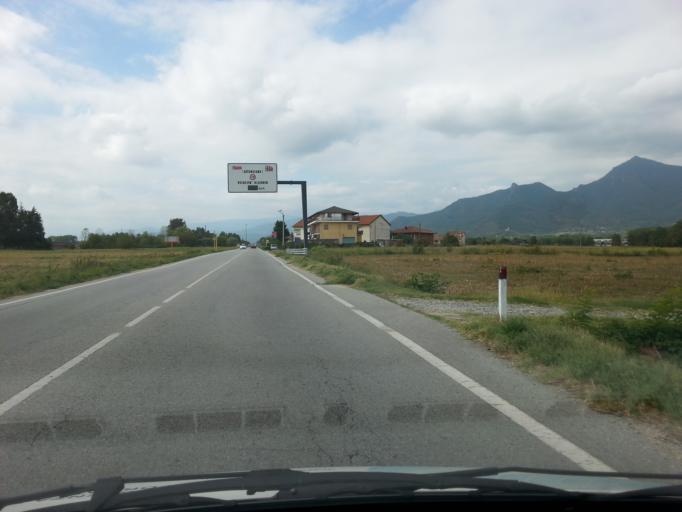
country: IT
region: Piedmont
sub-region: Provincia di Torino
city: Piossasco
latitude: 44.9641
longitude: 7.4224
